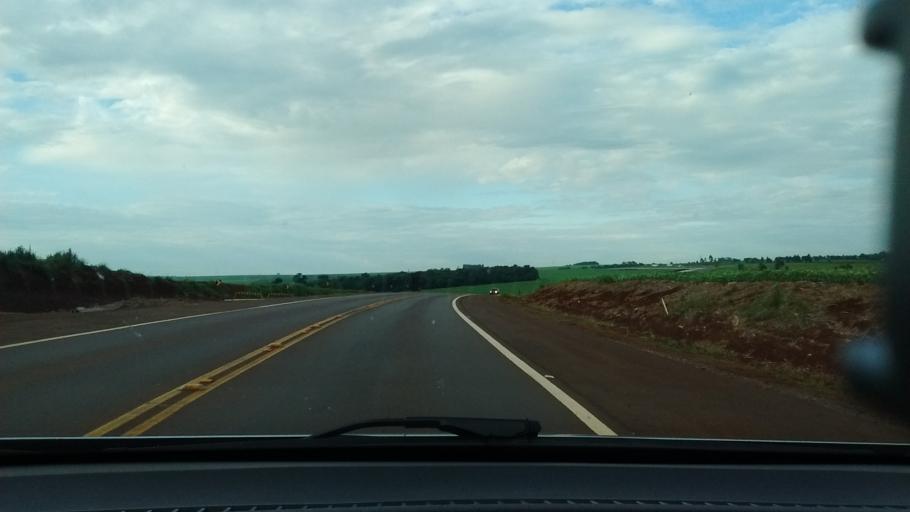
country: BR
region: Parana
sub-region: Cascavel
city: Cascavel
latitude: -25.0306
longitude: -53.5483
